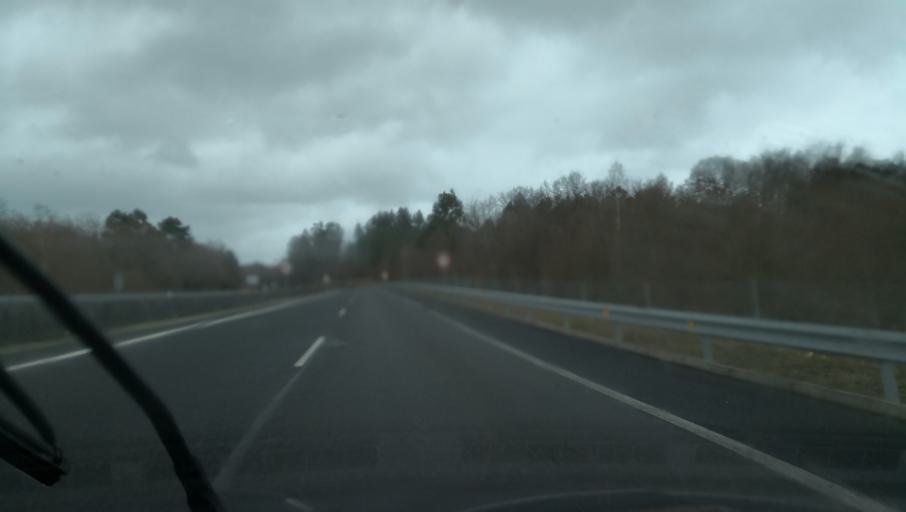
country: ES
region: Galicia
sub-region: Provincia de Pontevedra
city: Lalin
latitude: 42.6782
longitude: -8.1625
